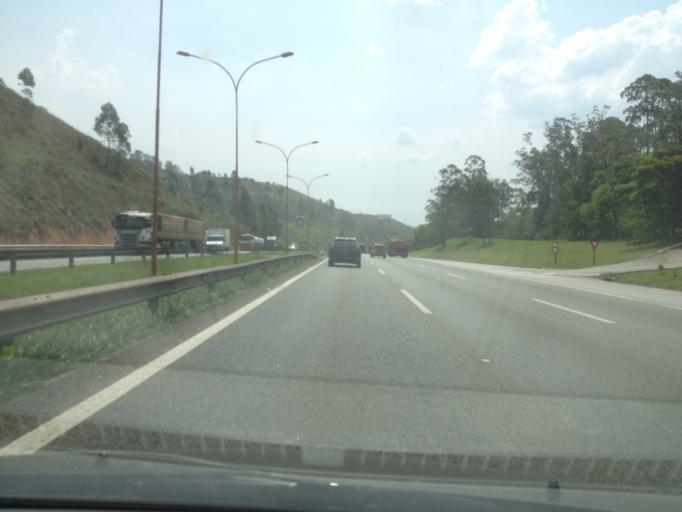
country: BR
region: Sao Paulo
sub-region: Pirapora Do Bom Jesus
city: Pirapora do Bom Jesus
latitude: -23.4587
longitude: -47.0463
